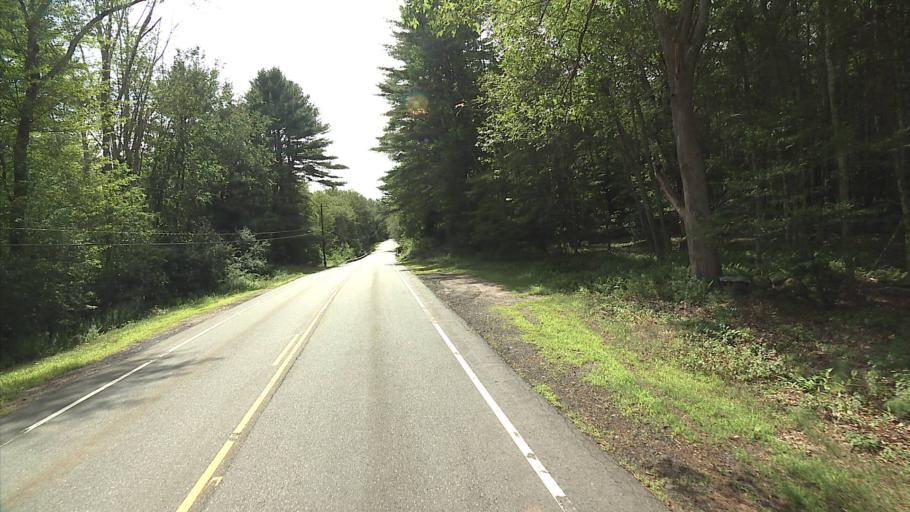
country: US
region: Connecticut
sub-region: Windham County
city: South Woodstock
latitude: 41.9376
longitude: -72.0975
